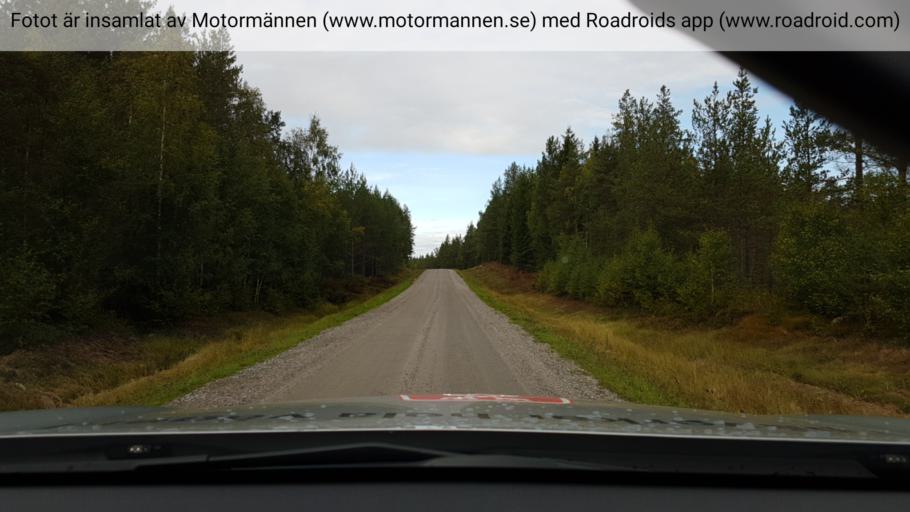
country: SE
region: Vaesterbotten
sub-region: Skelleftea Kommun
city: Byske
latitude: 65.1381
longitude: 21.1855
